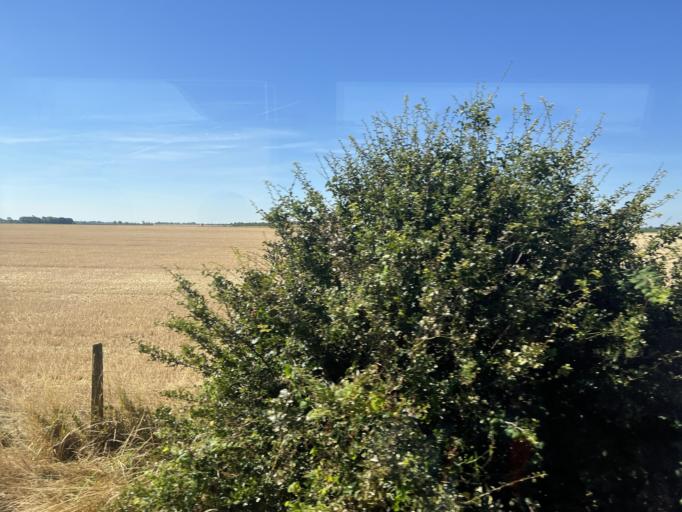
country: GB
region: England
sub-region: Lincolnshire
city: Heckington
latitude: 52.9836
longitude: -0.3265
